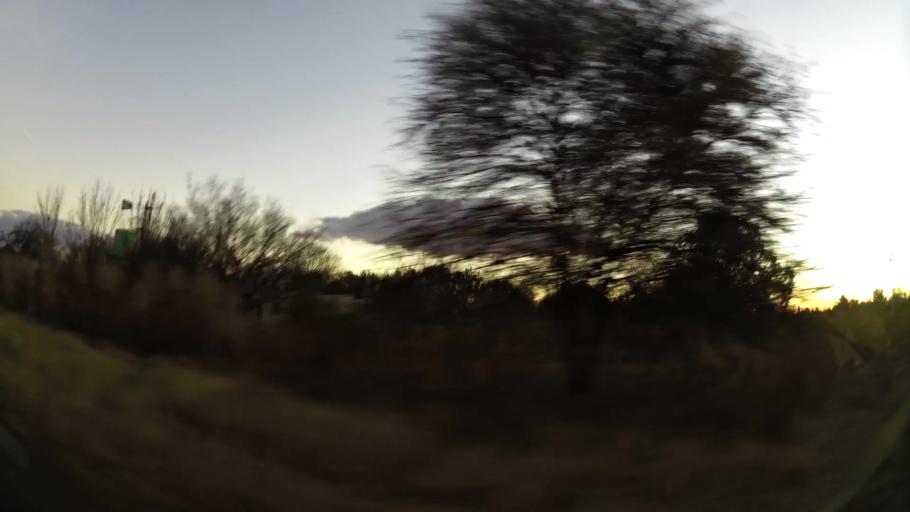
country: ZA
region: North-West
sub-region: Dr Kenneth Kaunda District Municipality
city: Potchefstroom
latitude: -26.7089
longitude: 27.1265
